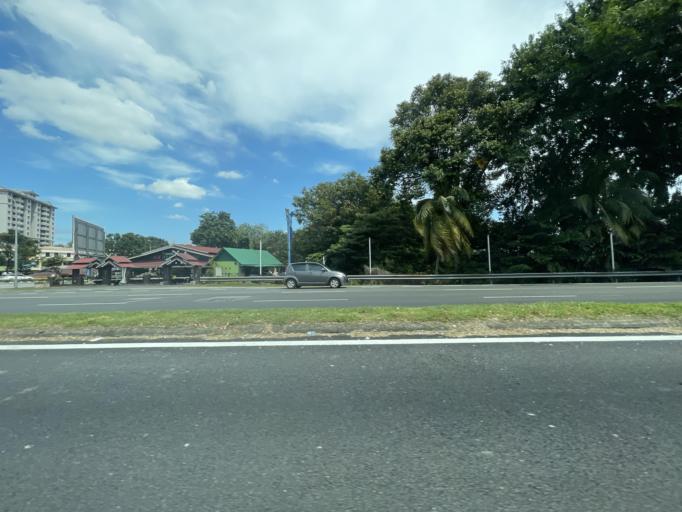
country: MY
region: Melaka
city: Batu Berendam
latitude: 2.2449
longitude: 102.2232
